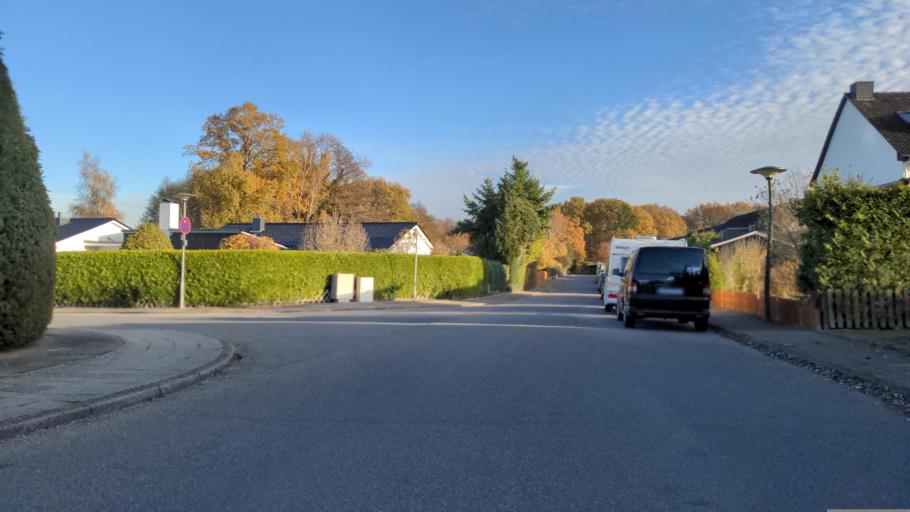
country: DE
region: Schleswig-Holstein
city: Gross Gronau
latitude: 53.8403
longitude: 10.7446
